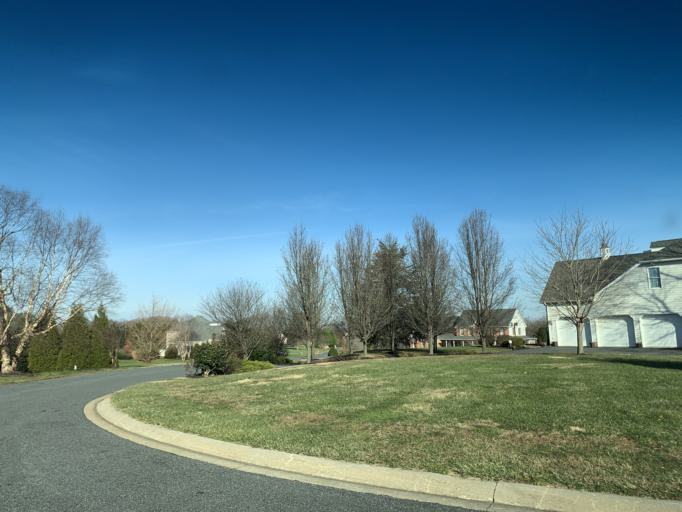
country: US
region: Maryland
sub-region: Harford County
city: South Bel Air
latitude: 39.5681
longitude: -76.2522
